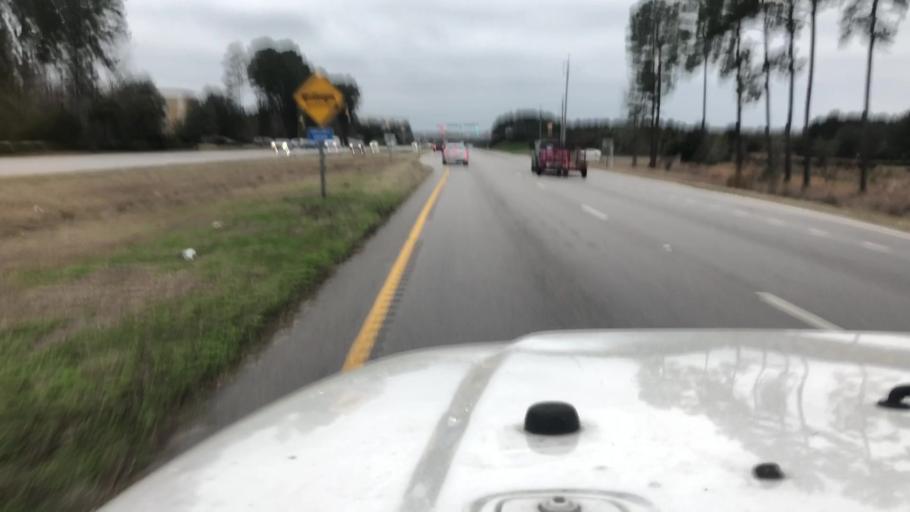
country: US
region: South Carolina
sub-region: Beaufort County
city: Bluffton
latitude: 32.2984
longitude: -80.9454
